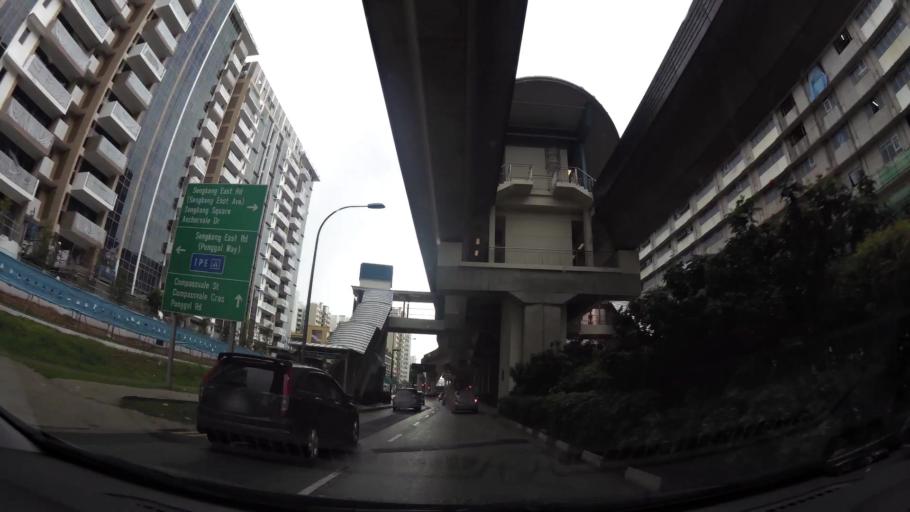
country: MY
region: Johor
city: Kampung Pasir Gudang Baru
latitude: 1.3965
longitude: 103.8935
